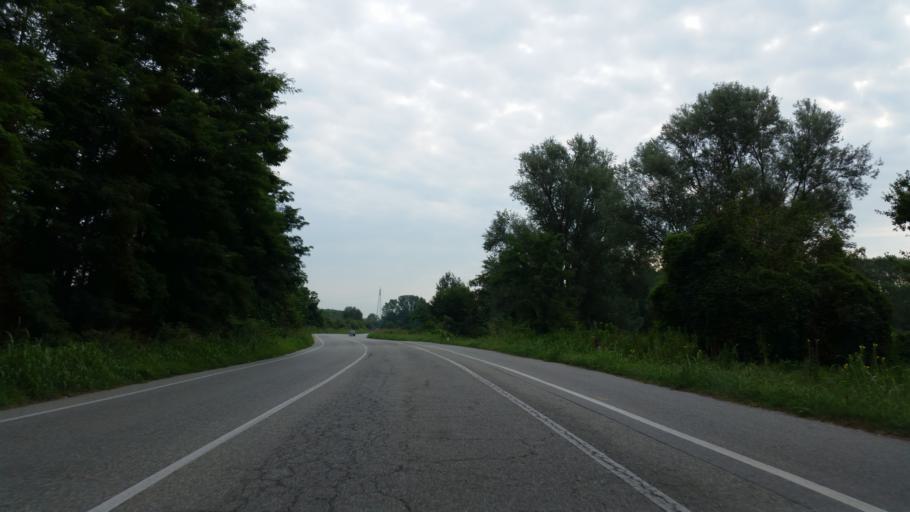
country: IT
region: Piedmont
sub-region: Provincia di Torino
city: San Sebastiano da Po
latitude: 45.1798
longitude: 7.9528
